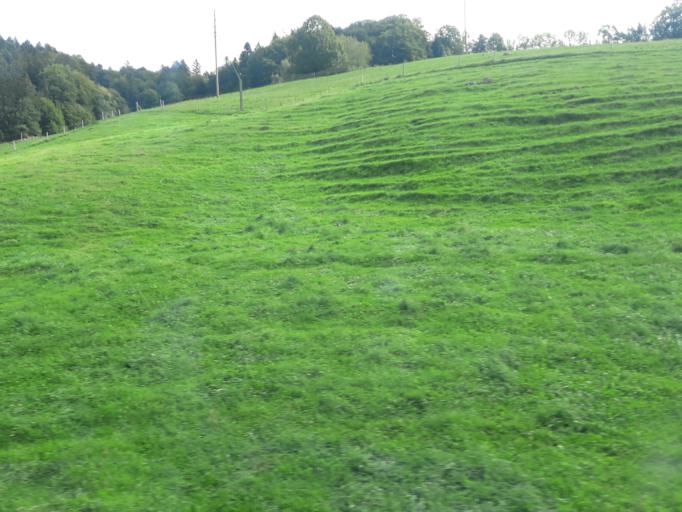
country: CH
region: Bern
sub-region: Bern-Mittelland District
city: Wahlern
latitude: 46.8557
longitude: 7.3631
